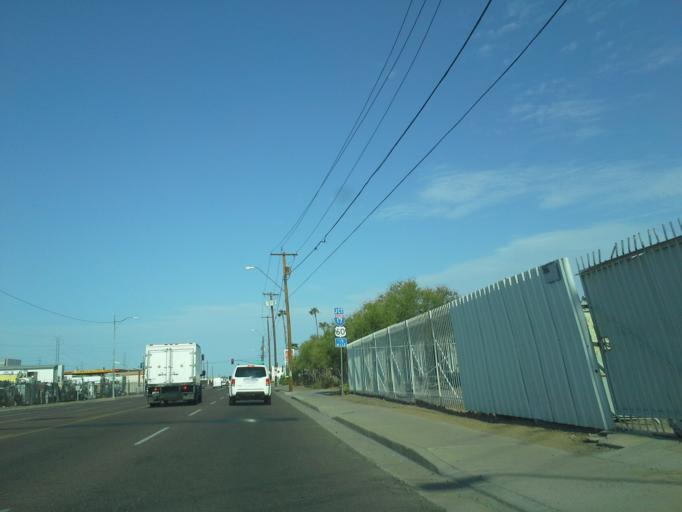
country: US
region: Arizona
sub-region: Maricopa County
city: Phoenix
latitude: 33.4415
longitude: -112.0983
